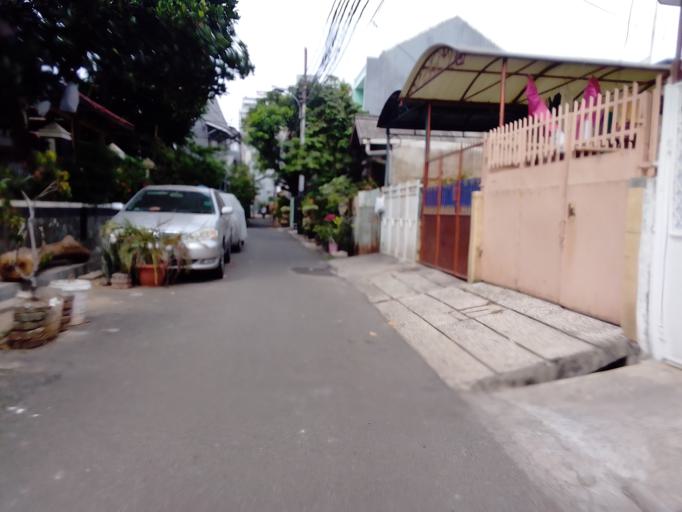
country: ID
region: Jakarta Raya
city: Jakarta
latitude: -6.1640
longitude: 106.8091
